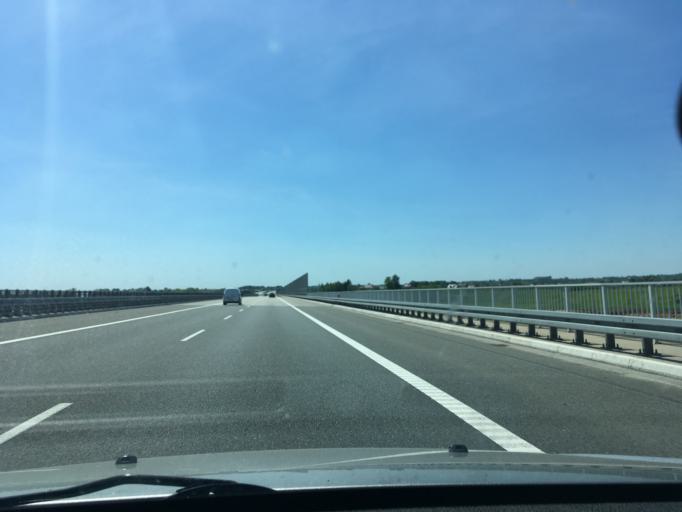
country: PL
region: Subcarpathian Voivodeship
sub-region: Powiat debicki
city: Zyrakow
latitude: 50.0855
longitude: 21.4228
